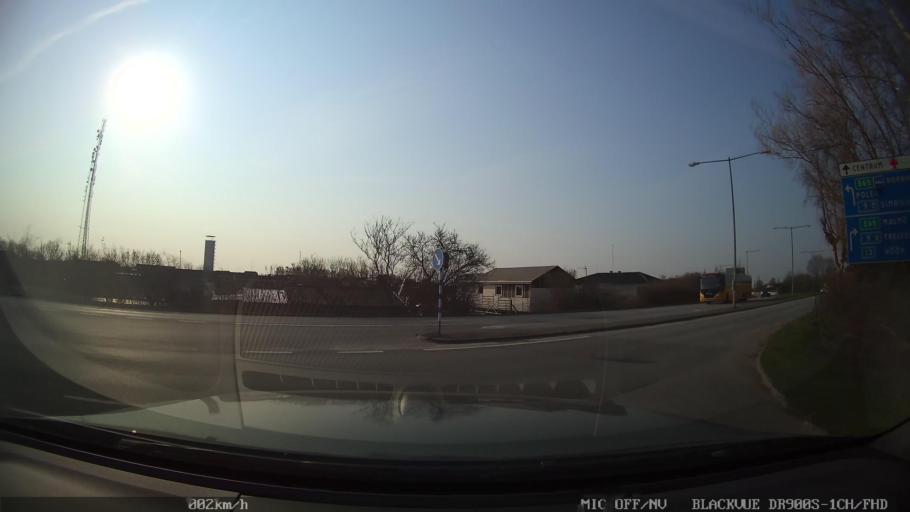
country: SE
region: Skane
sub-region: Ystads Kommun
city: Ystad
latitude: 55.4439
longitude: 13.8367
